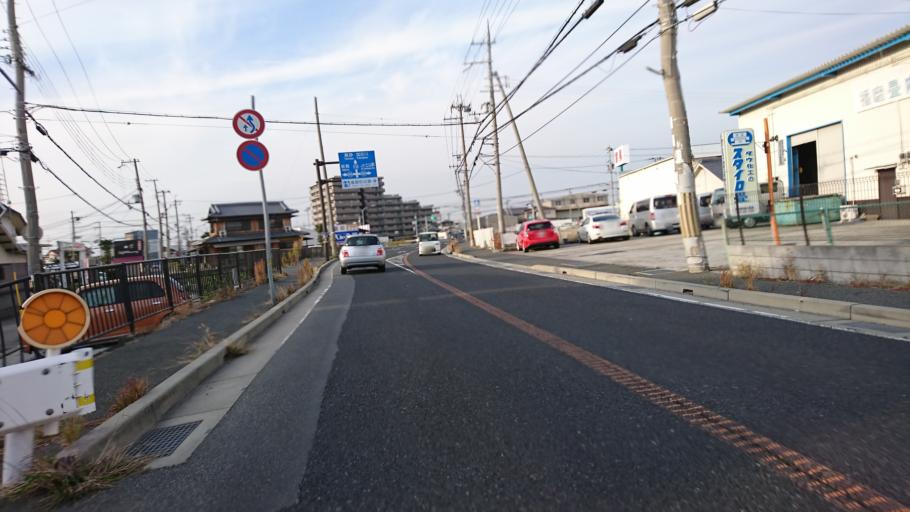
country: JP
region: Hyogo
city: Kakogawacho-honmachi
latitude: 34.7122
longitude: 134.8631
